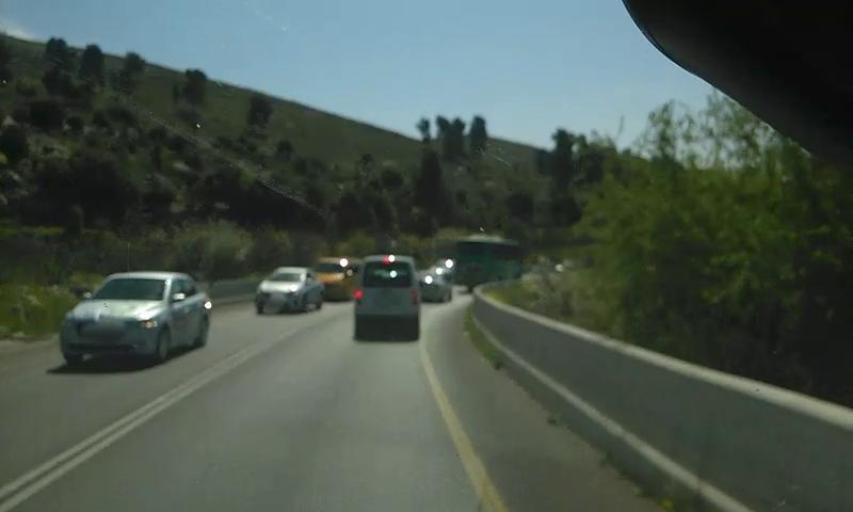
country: PS
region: West Bank
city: Shuyukh al `Arrub
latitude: 31.6375
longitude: 35.1328
